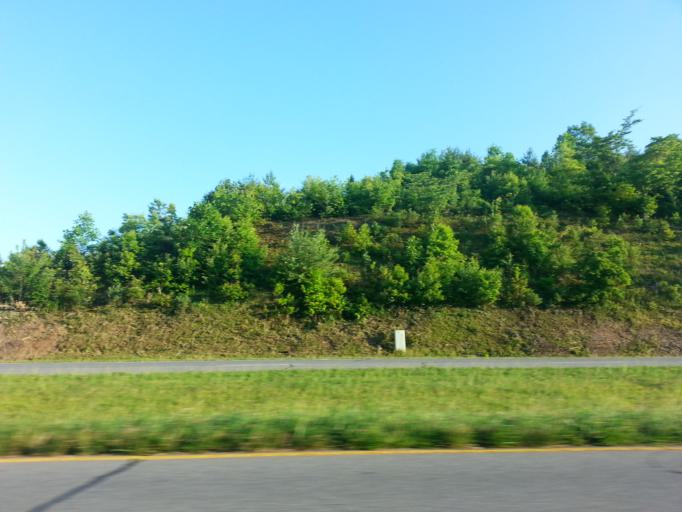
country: US
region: North Carolina
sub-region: Cherokee County
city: Murphy
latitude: 35.0257
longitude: -84.1254
